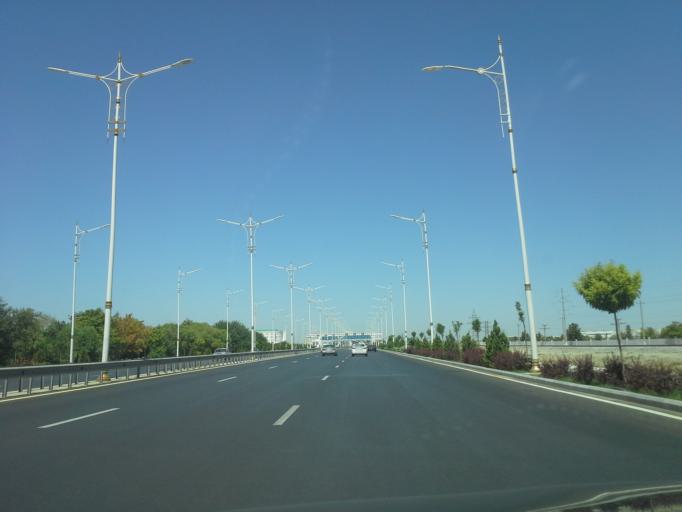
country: TM
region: Ahal
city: Ashgabat
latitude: 37.9721
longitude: 58.3500
